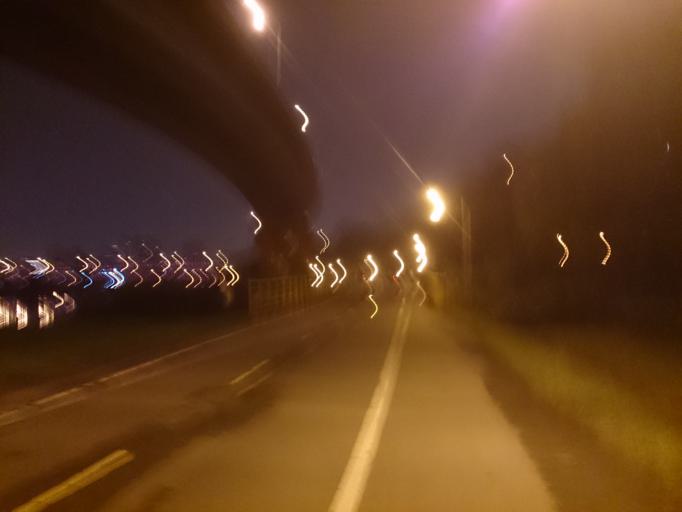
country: TW
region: Taipei
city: Taipei
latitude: 25.0093
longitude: 121.5324
